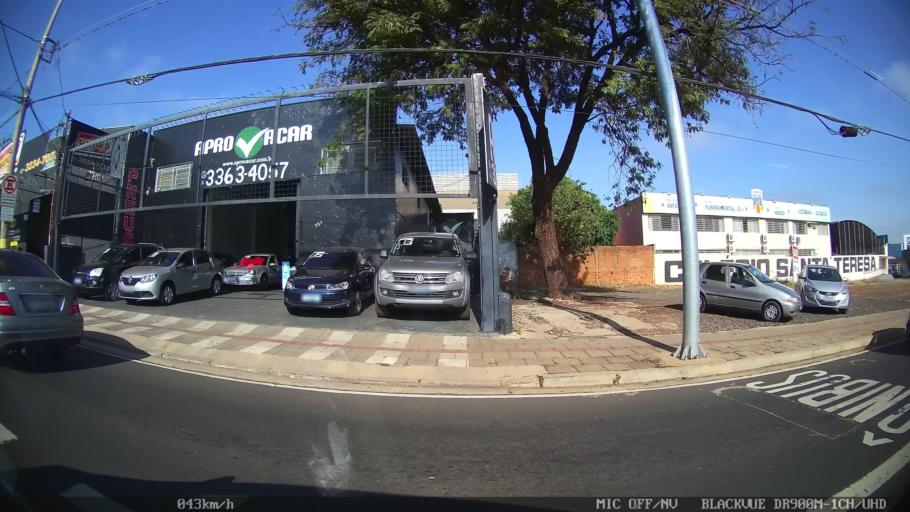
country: BR
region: Sao Paulo
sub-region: Sao Jose Do Rio Preto
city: Sao Jose do Rio Preto
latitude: -20.8046
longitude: -49.4044
